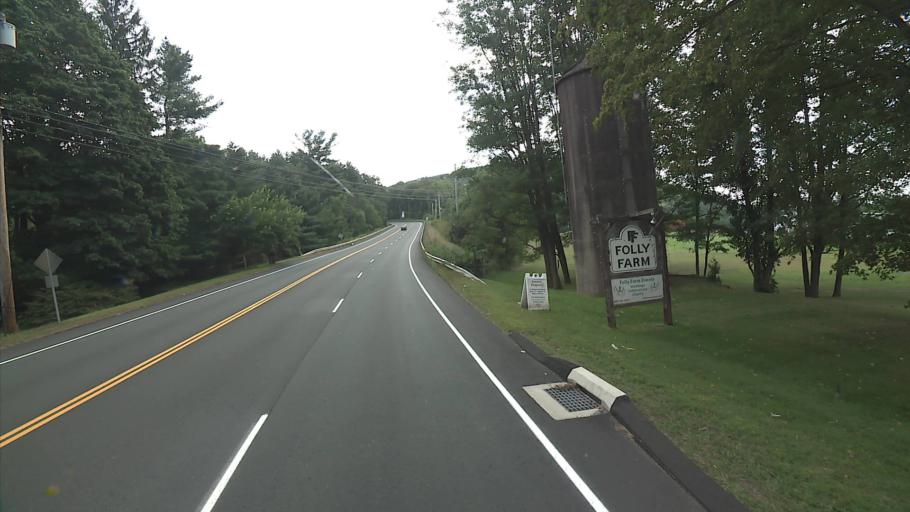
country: US
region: Connecticut
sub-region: Hartford County
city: Weatogue
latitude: 41.8470
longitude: -72.8000
